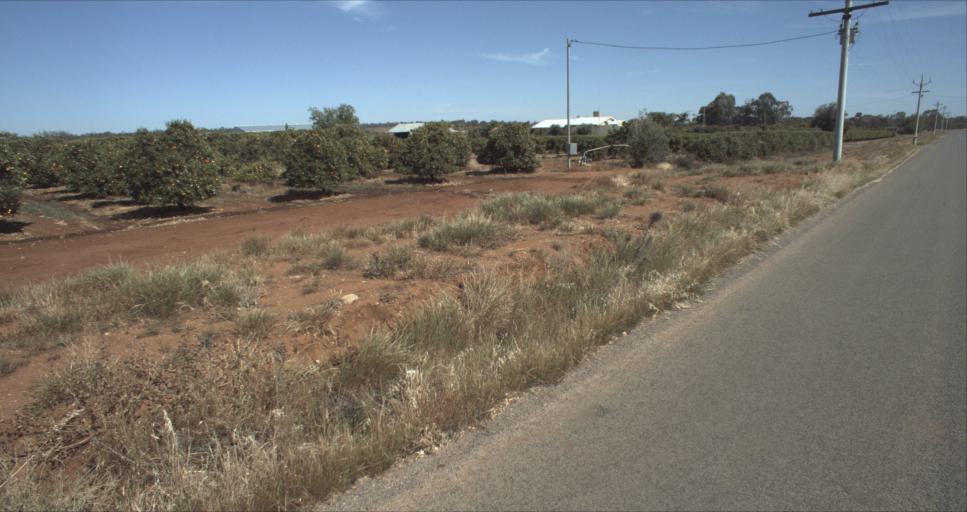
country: AU
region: New South Wales
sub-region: Leeton
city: Leeton
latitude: -34.5831
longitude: 146.4705
